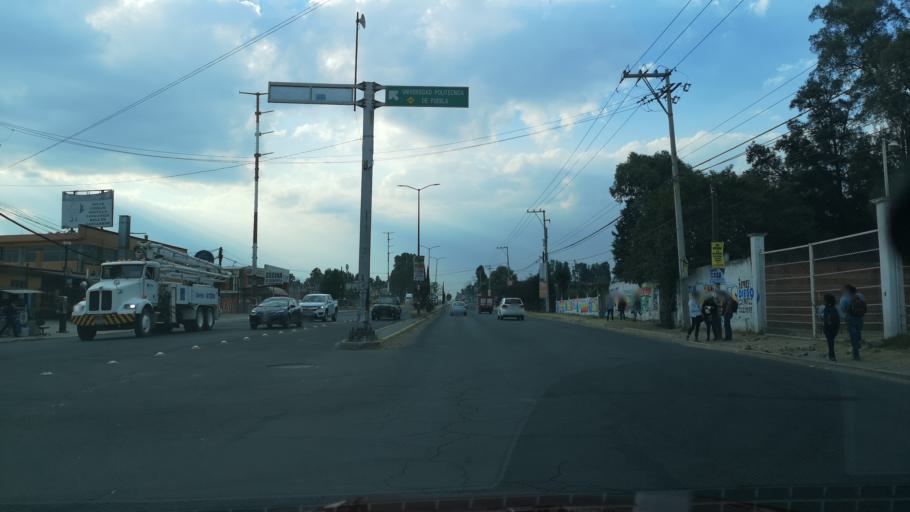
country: MX
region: Puebla
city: Cuanala
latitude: 19.1019
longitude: -98.3464
